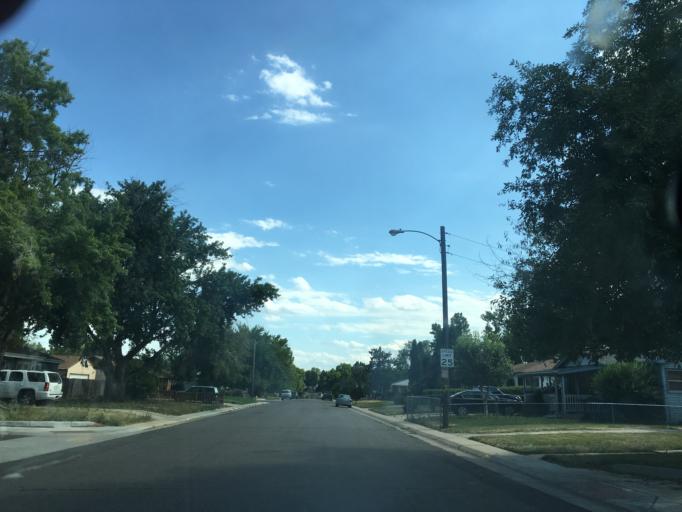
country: US
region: Colorado
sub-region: Arapahoe County
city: Sheridan
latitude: 39.6885
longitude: -105.0391
